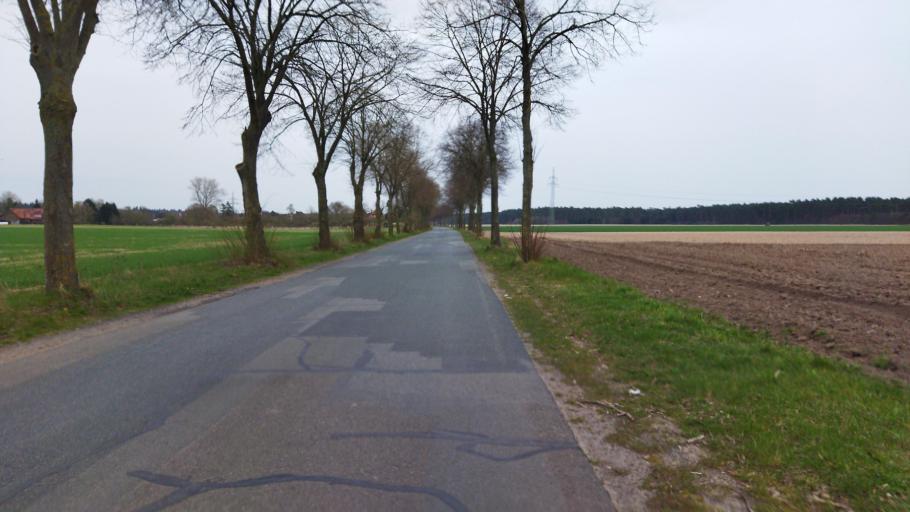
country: DE
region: Lower Saxony
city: Estorf
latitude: 52.5964
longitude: 9.1745
